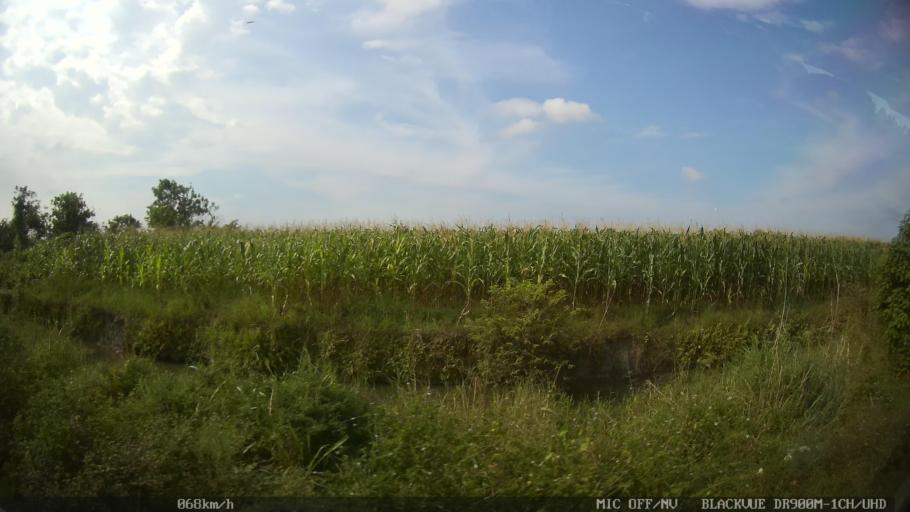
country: ID
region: North Sumatra
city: Medan
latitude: 3.5731
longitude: 98.7673
